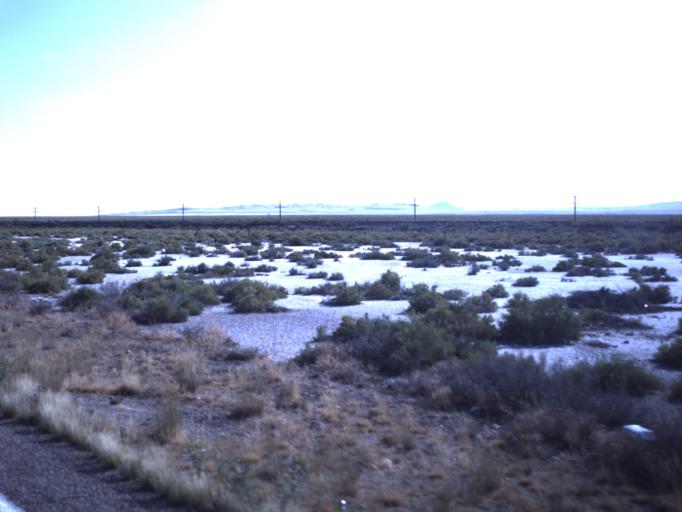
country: US
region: Utah
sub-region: Beaver County
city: Milford
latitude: 38.6041
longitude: -112.9869
